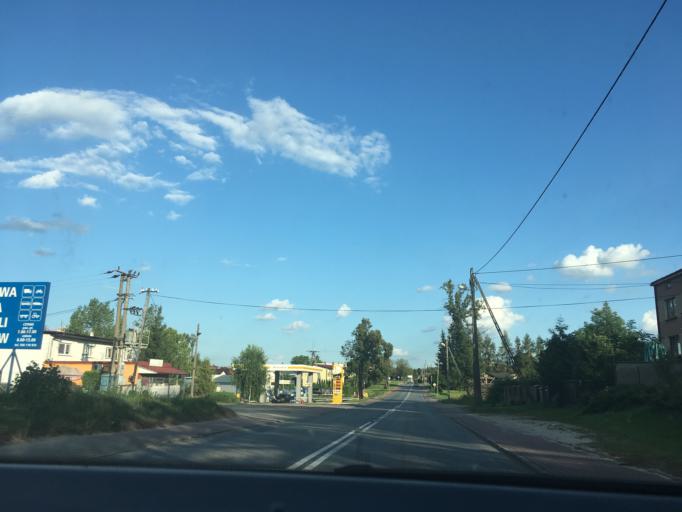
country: PL
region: Masovian Voivodeship
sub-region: Powiat losicki
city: Sarnaki
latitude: 52.3203
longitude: 22.8826
